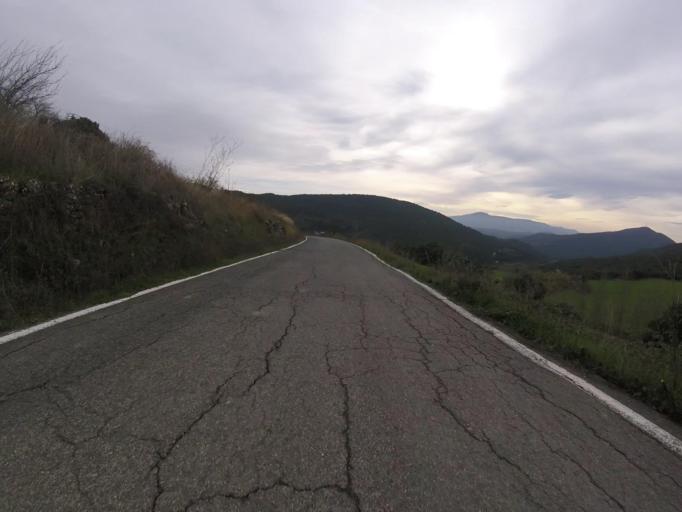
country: ES
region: Navarre
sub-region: Provincia de Navarra
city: Estella
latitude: 42.7156
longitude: -2.0492
